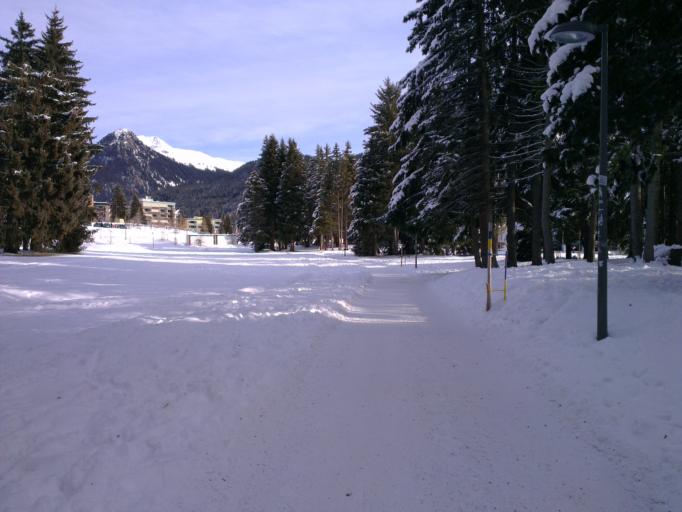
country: CH
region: Grisons
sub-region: Praettigau/Davos District
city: Davos
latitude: 46.7991
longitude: 9.8293
